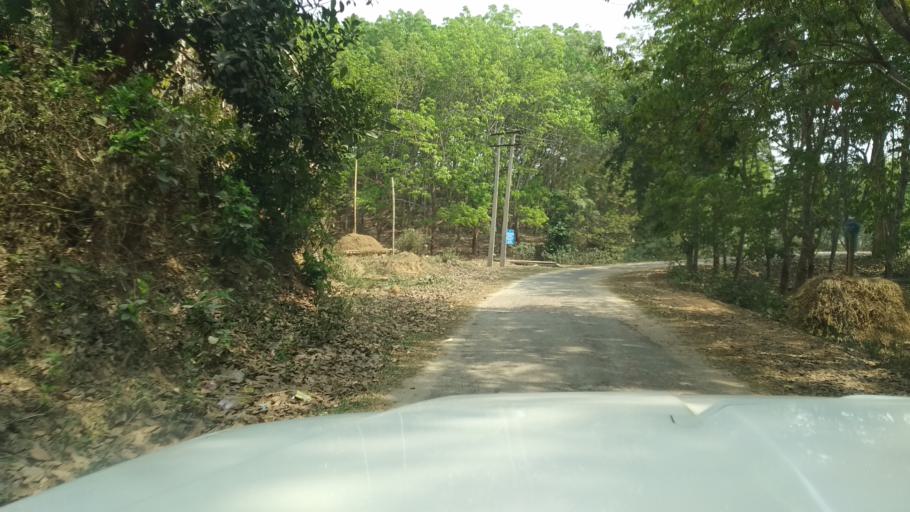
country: IN
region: Tripura
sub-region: West Tripura
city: Sonamura
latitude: 23.4288
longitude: 91.3171
